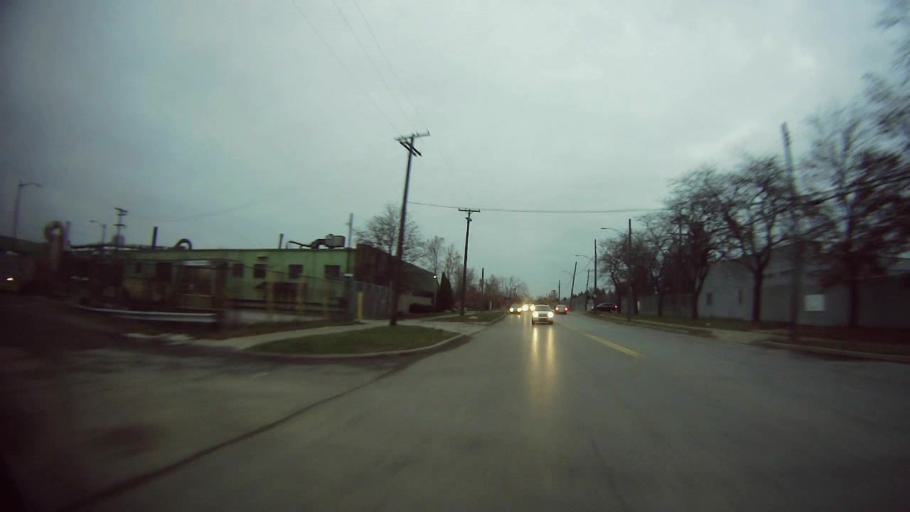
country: US
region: Michigan
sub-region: Wayne County
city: Hamtramck
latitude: 42.4217
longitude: -83.0626
